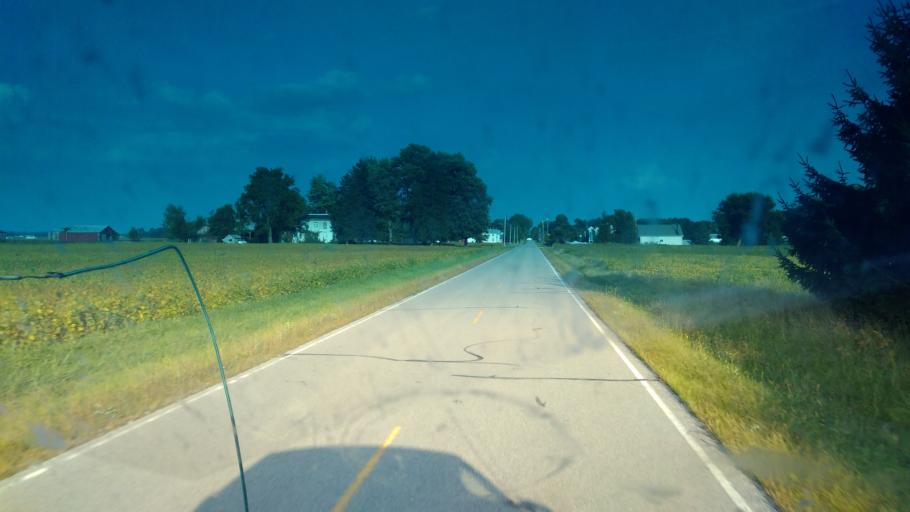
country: US
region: Ohio
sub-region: Crawford County
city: Bucyrus
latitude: 40.9649
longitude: -83.0252
